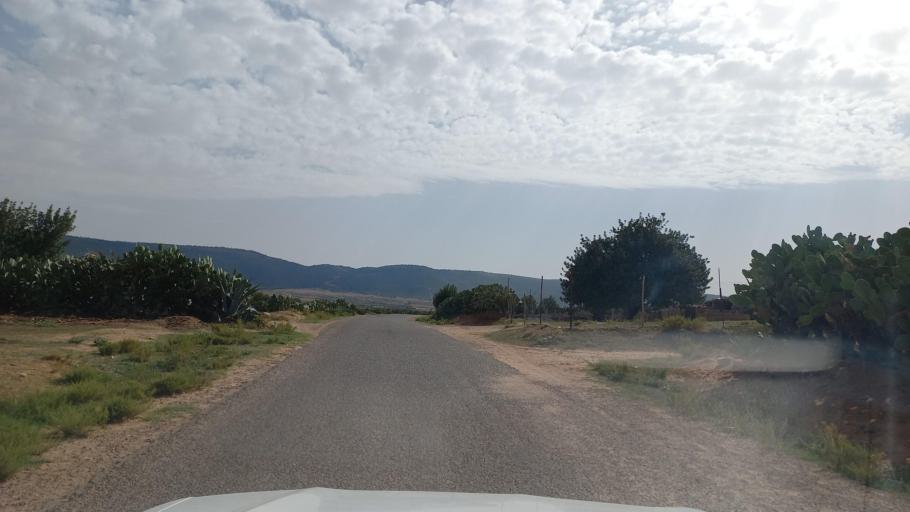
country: TN
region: Al Qasrayn
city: Kasserine
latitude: 35.3650
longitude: 8.8550
